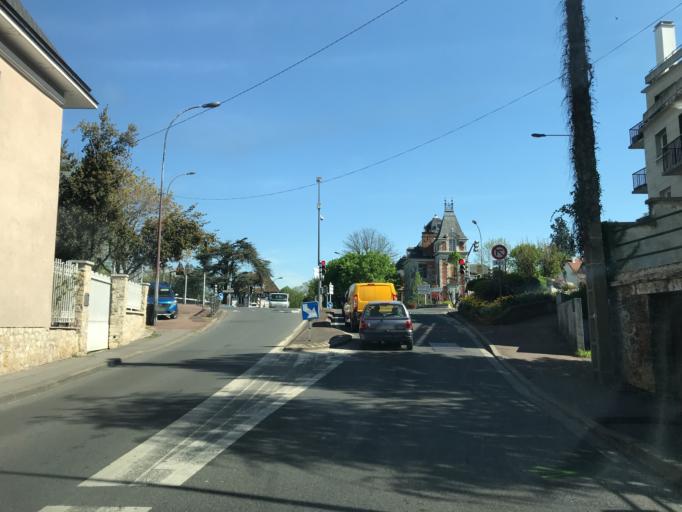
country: FR
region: Ile-de-France
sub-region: Departement du Val-de-Marne
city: Chennevieres-sur-Marne
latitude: 48.7897
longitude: 2.5221
